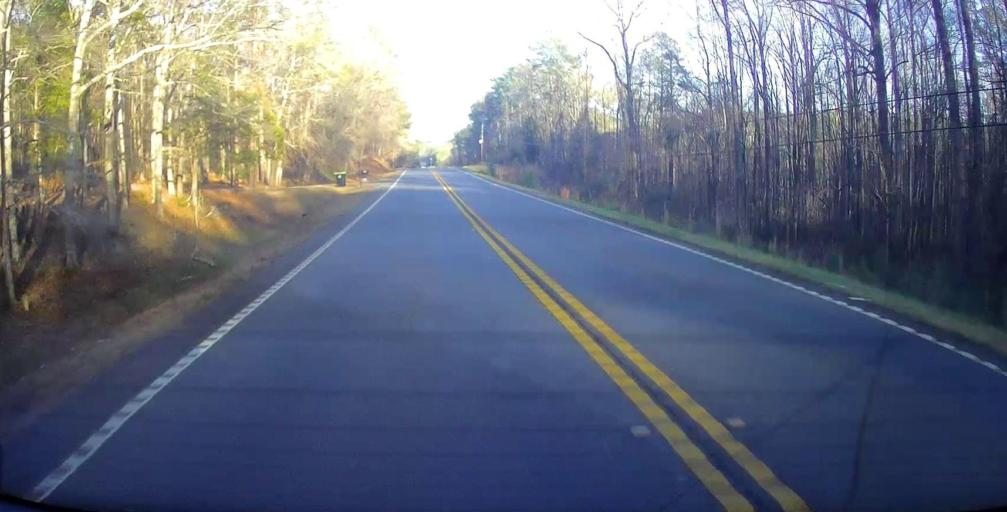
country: US
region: Georgia
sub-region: Upson County
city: Thomaston
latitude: 32.8788
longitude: -84.3827
